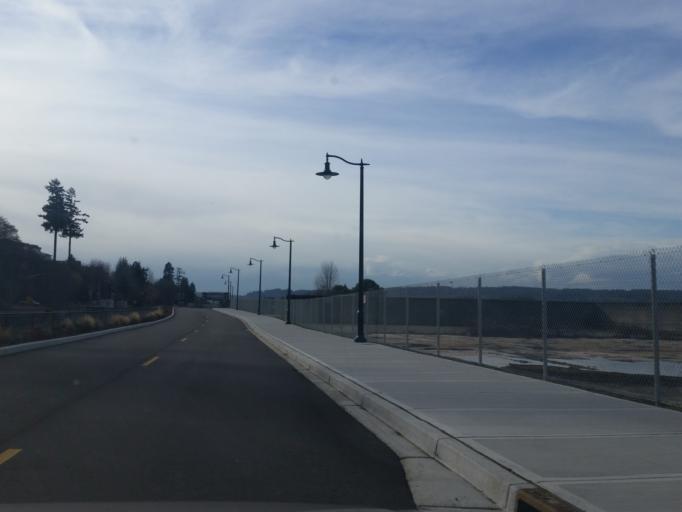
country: US
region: Washington
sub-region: Snohomish County
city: Mukilteo
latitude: 47.9514
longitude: -122.2913
